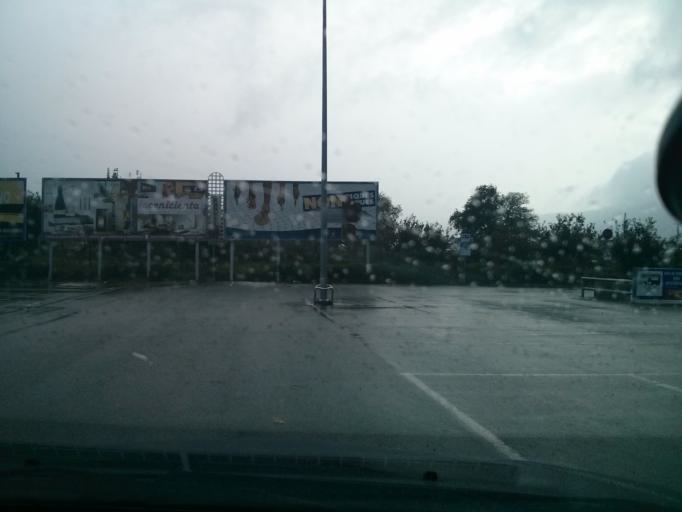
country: ES
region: Galicia
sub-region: Provincia da Coruna
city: Noia
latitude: 42.7974
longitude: -8.8884
